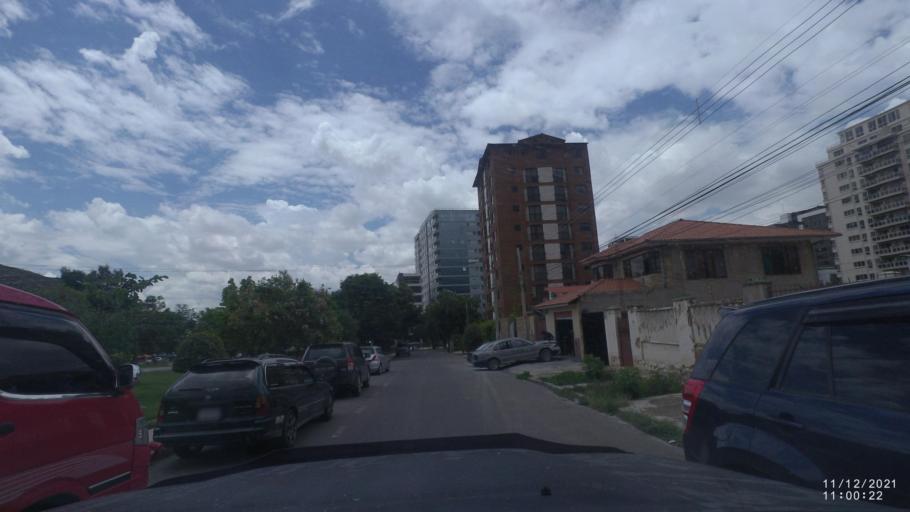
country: BO
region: Cochabamba
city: Cochabamba
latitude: -17.3725
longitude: -66.1450
